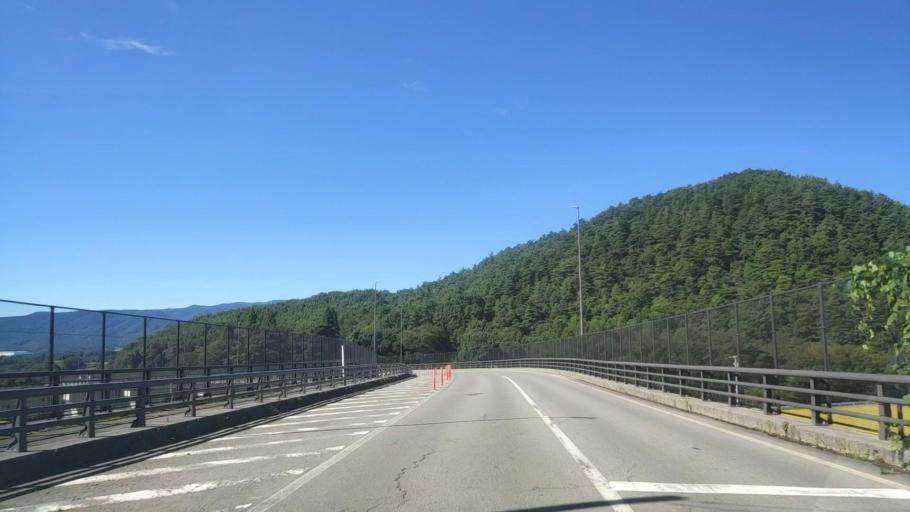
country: JP
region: Nagano
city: Chino
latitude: 35.9927
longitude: 138.2152
